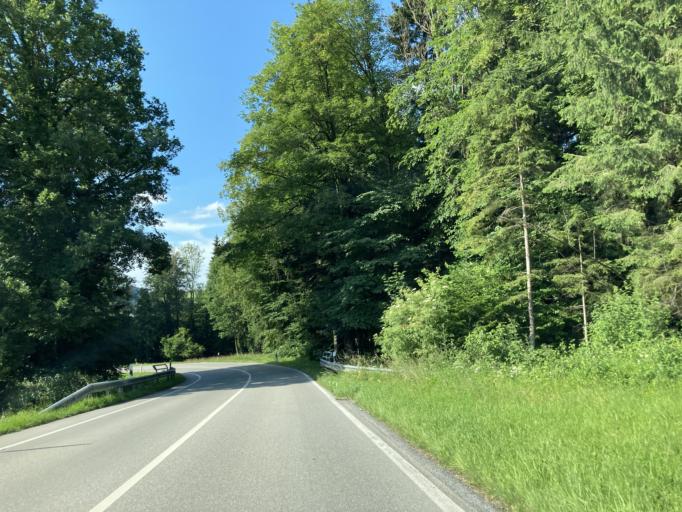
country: DE
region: Bavaria
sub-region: Upper Bavaria
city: Samerberg
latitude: 47.7908
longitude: 12.2349
